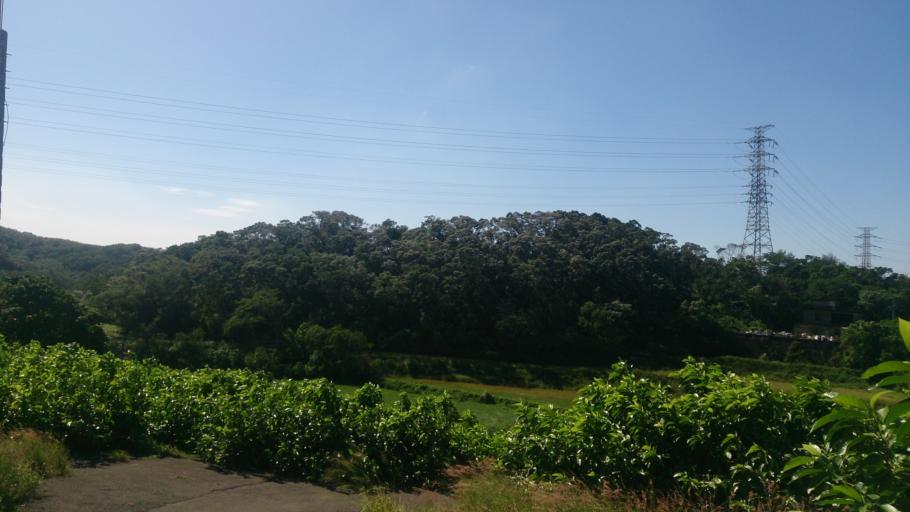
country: TW
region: Taiwan
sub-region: Hsinchu
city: Hsinchu
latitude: 24.7513
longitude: 120.9518
